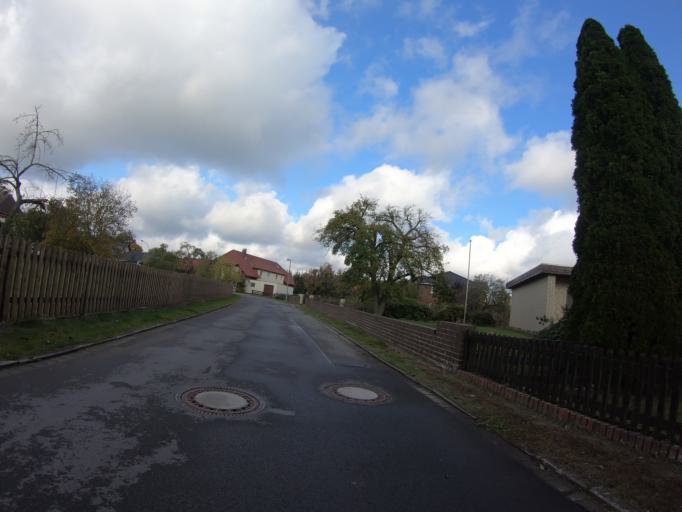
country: DE
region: Lower Saxony
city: Wagenhoff
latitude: 52.5204
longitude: 10.5406
